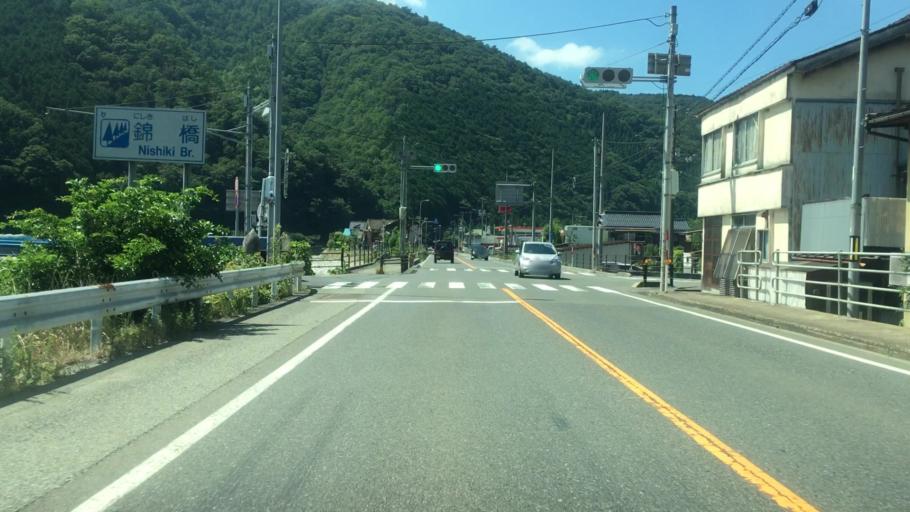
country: JP
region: Tottori
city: Tottori
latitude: 35.2701
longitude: 134.2274
